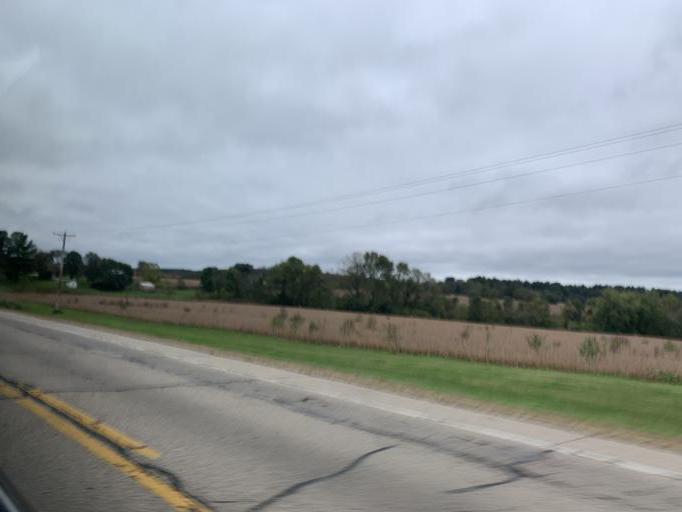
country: US
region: Wisconsin
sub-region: Grant County
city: Muscoda
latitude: 43.2198
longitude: -90.5379
